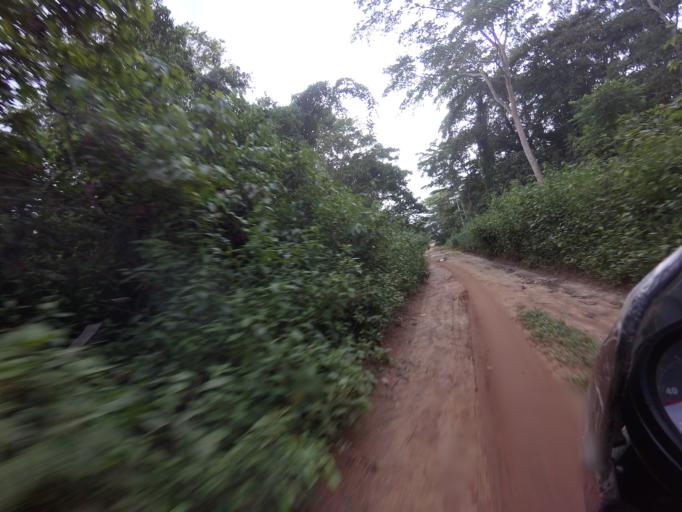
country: SL
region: Eastern Province
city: Jojoima
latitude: 7.8077
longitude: -10.8139
